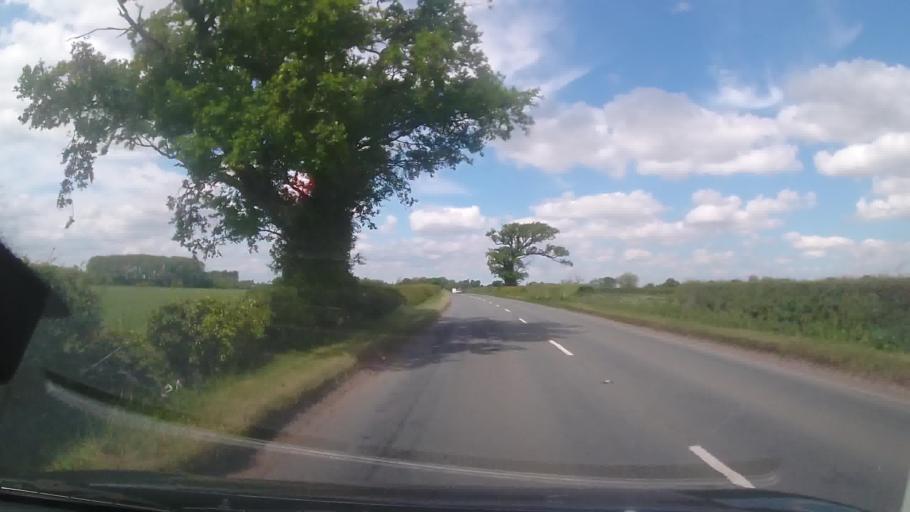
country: GB
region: England
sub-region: Telford and Wrekin
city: Eyton upon the Weald Moors
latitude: 52.7492
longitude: -2.5427
